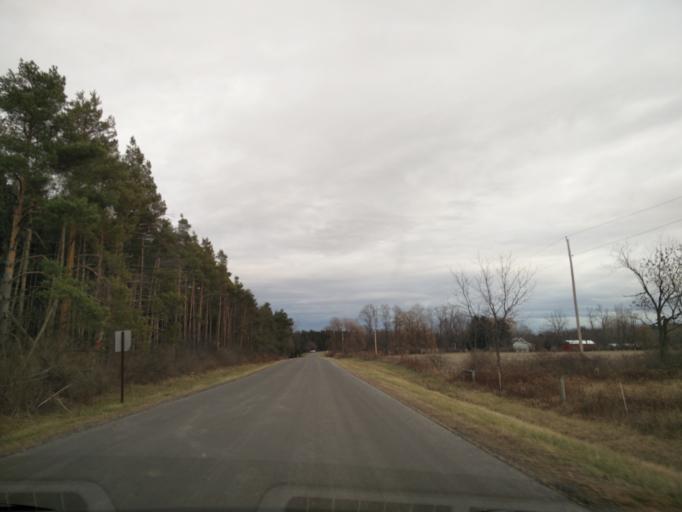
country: US
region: New York
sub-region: Tompkins County
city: Trumansburg
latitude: 42.5192
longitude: -76.6523
